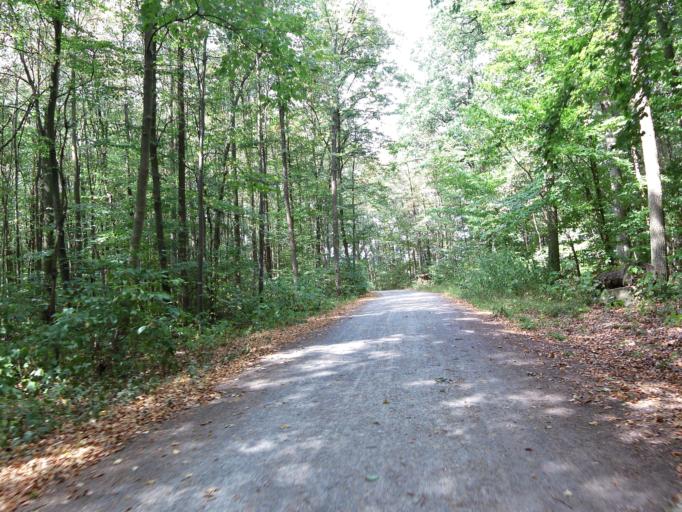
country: DE
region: Bavaria
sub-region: Regierungsbezirk Unterfranken
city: Gadheim
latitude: 49.8392
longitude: 9.8981
